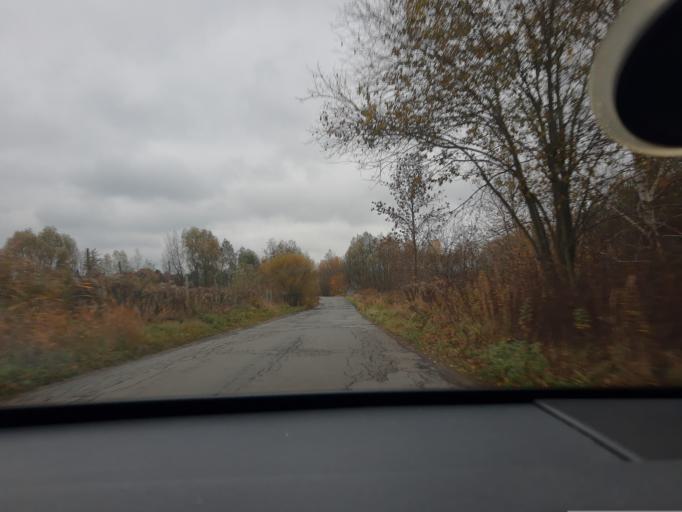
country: PL
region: Lodz Voivodeship
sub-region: Powiat pabianicki
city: Konstantynow Lodzki
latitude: 51.7483
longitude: 19.3718
